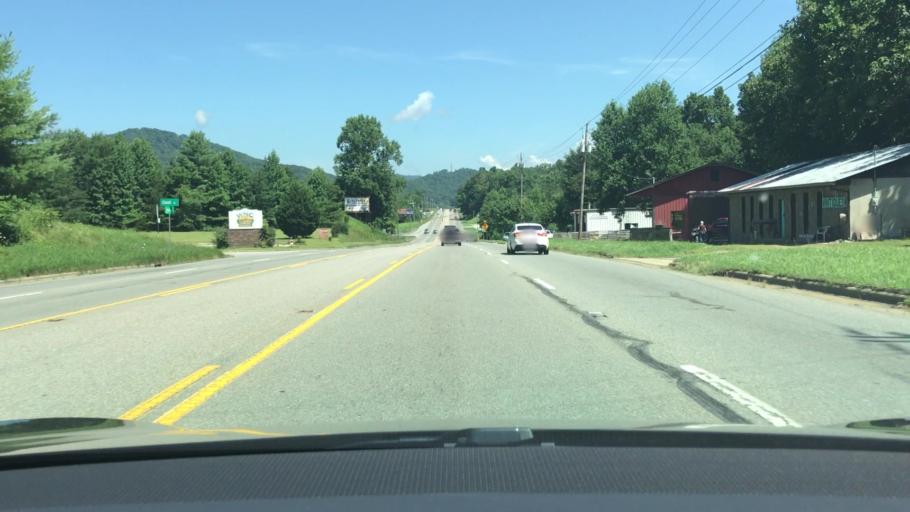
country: US
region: North Carolina
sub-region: Macon County
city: Franklin
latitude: 35.1180
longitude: -83.3915
